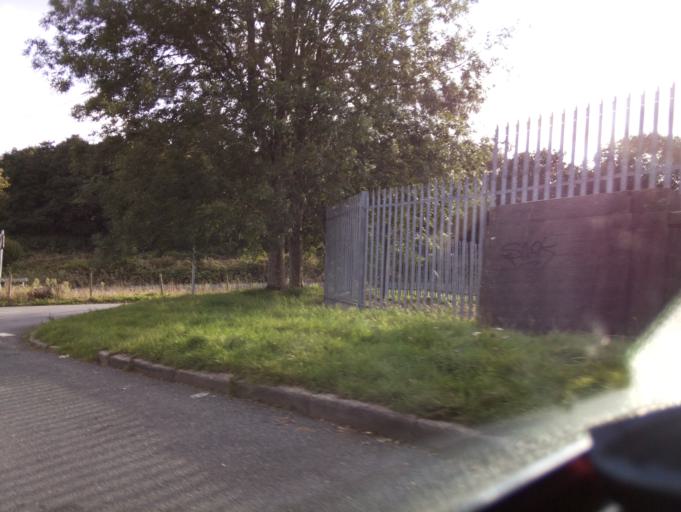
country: GB
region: Wales
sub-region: Caerphilly County Borough
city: Abertridwr
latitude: 51.5714
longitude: -3.2952
